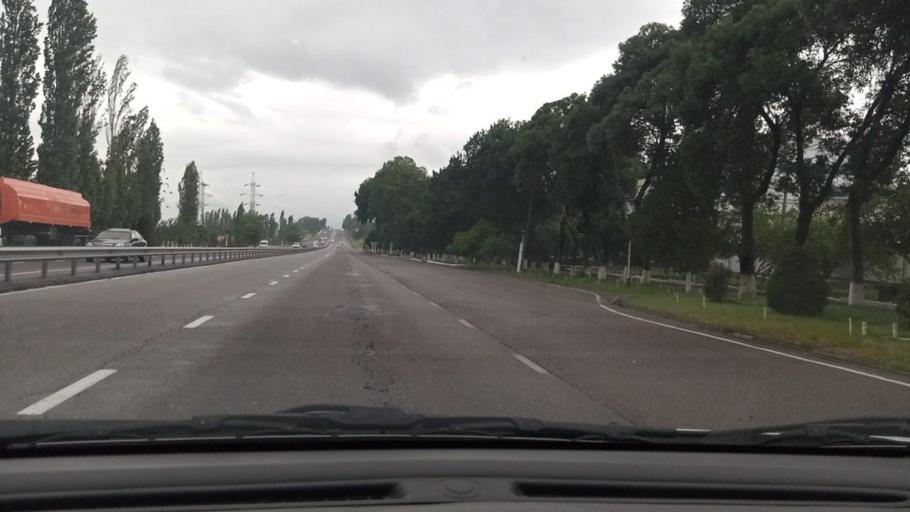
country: UZ
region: Toshkent
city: Angren
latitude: 40.9770
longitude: 70.0059
